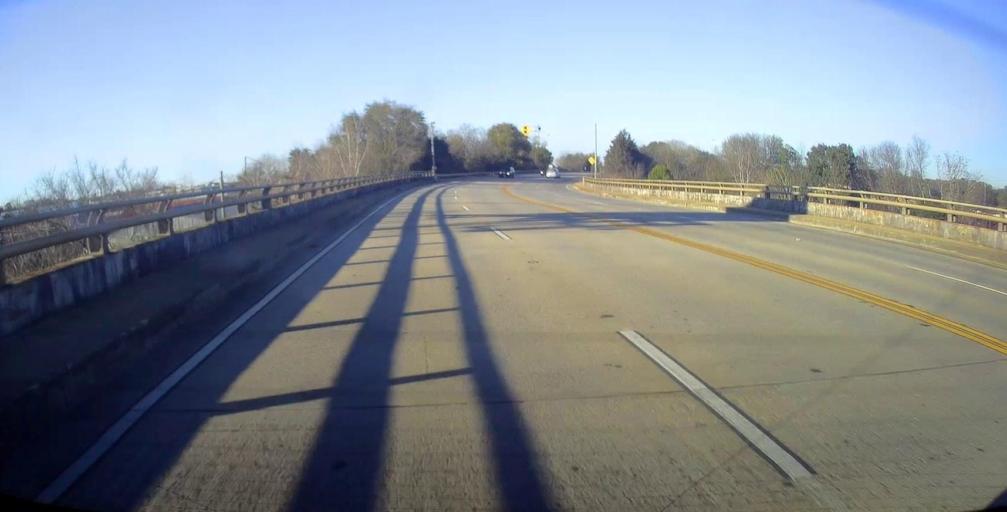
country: US
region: Georgia
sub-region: Dougherty County
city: Albany
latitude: 31.6022
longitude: -84.1562
